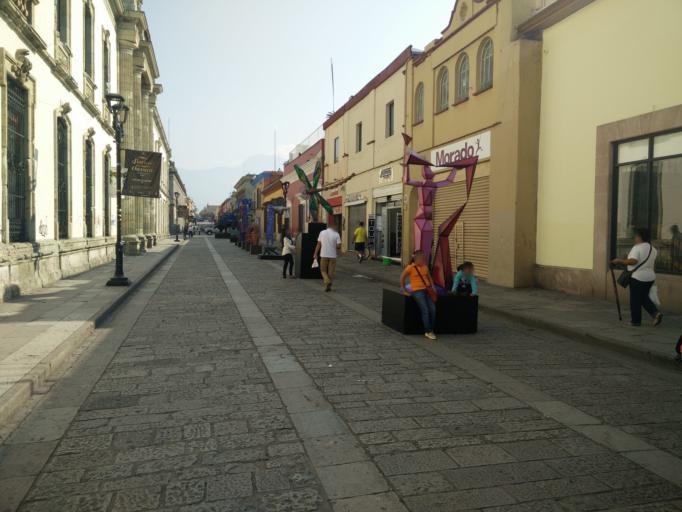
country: MX
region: Oaxaca
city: Oaxaca de Juarez
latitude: 17.0620
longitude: -96.7245
